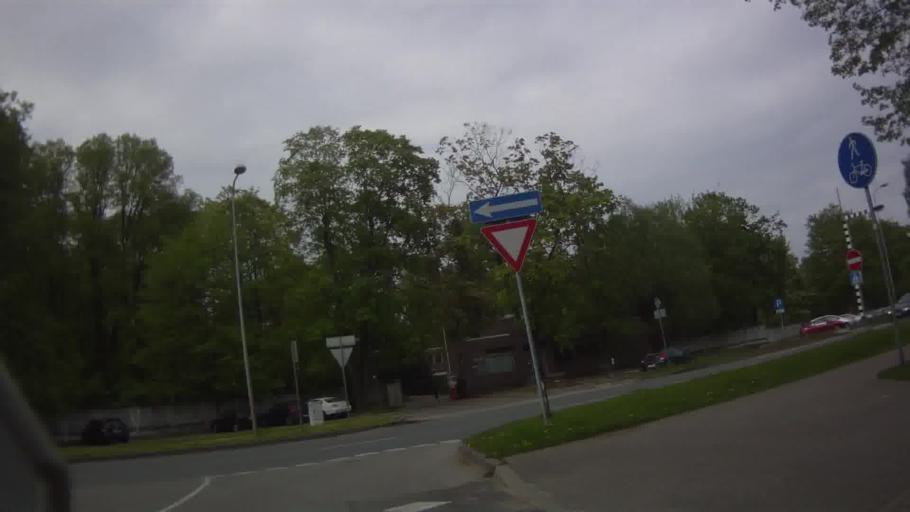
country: LV
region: Riga
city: Riga
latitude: 56.9761
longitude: 24.1390
